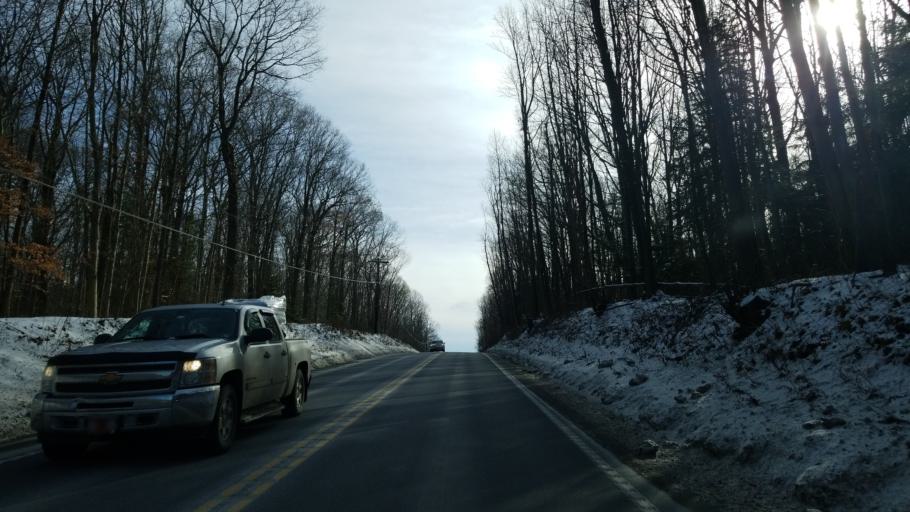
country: US
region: Pennsylvania
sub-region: Clearfield County
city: Clearfield
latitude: 41.1324
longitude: -78.5383
